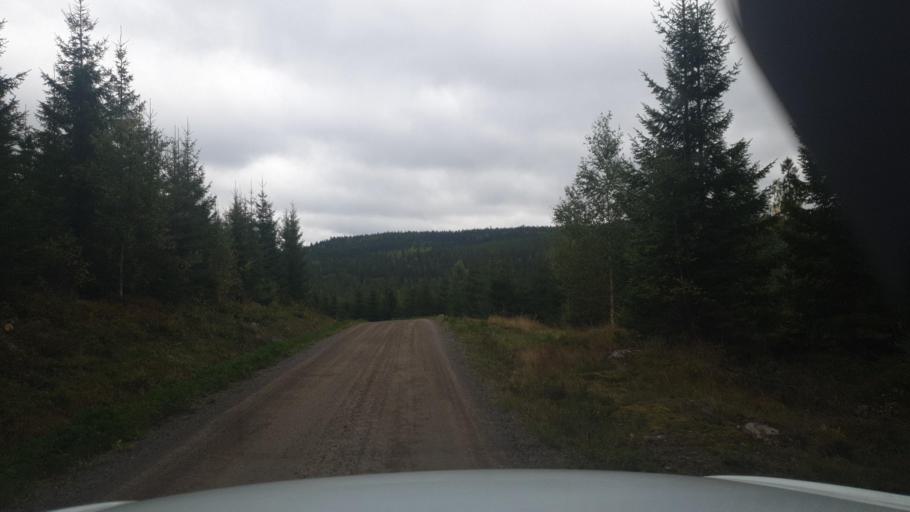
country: SE
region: Vaermland
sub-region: Sunne Kommun
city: Sunne
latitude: 59.8546
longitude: 12.8479
